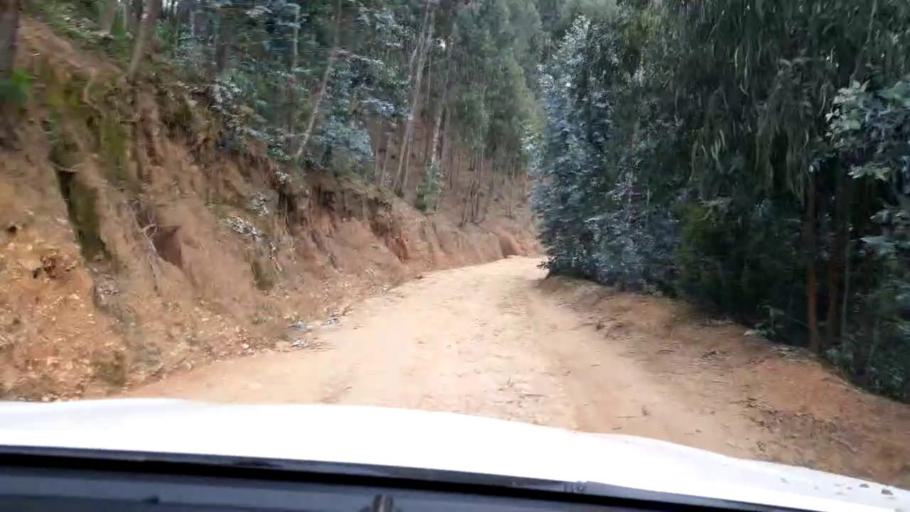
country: RW
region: Western Province
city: Kibuye
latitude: -1.8951
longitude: 29.5295
